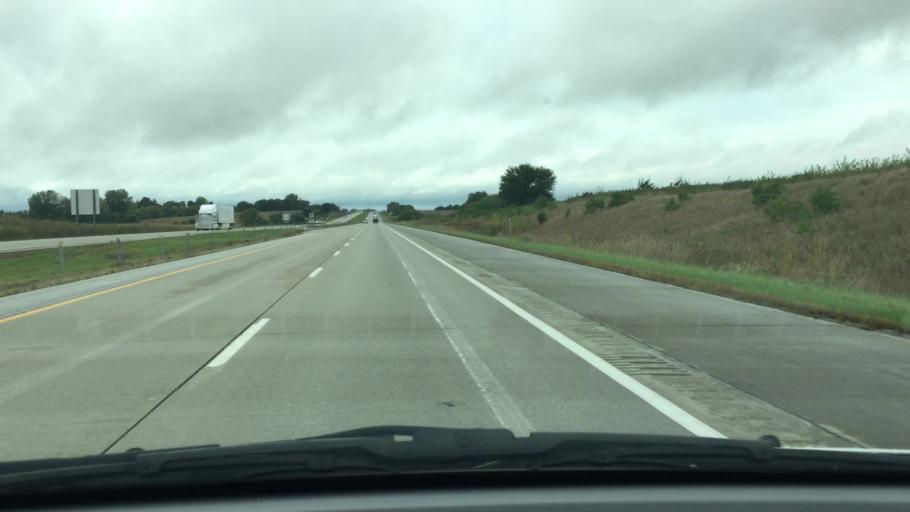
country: US
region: Iowa
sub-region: Polk County
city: Mitchellville
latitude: 41.6791
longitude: -93.4092
